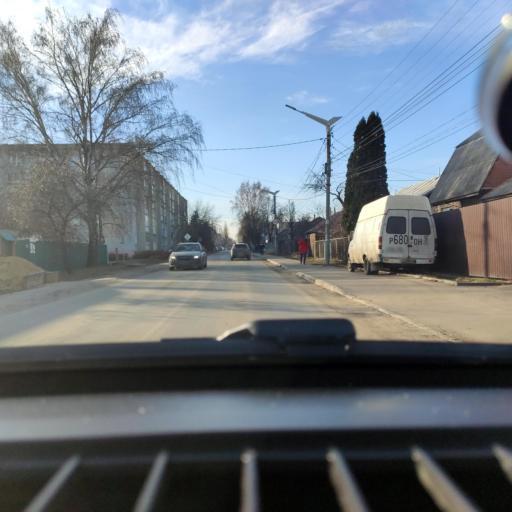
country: RU
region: Voronezj
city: Semiluki
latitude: 51.6974
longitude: 39.0225
